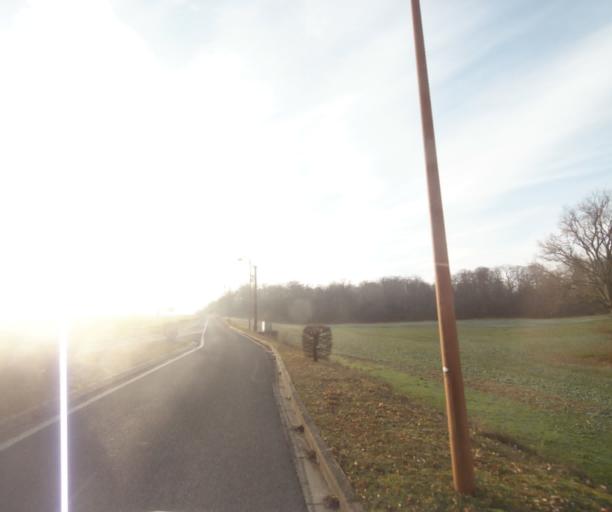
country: FR
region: Champagne-Ardenne
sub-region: Departement de la Haute-Marne
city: Chancenay
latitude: 48.7206
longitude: 4.9425
